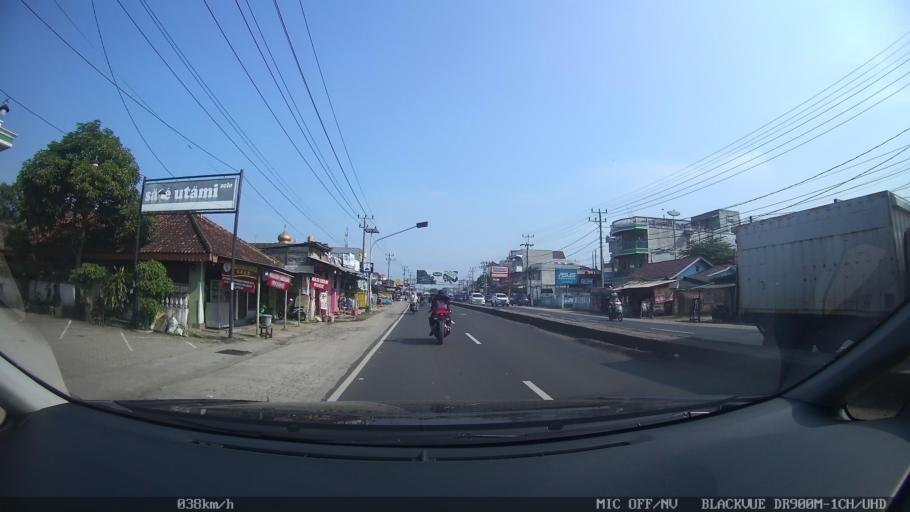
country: ID
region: Lampung
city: Natar
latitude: -5.3147
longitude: 105.1961
